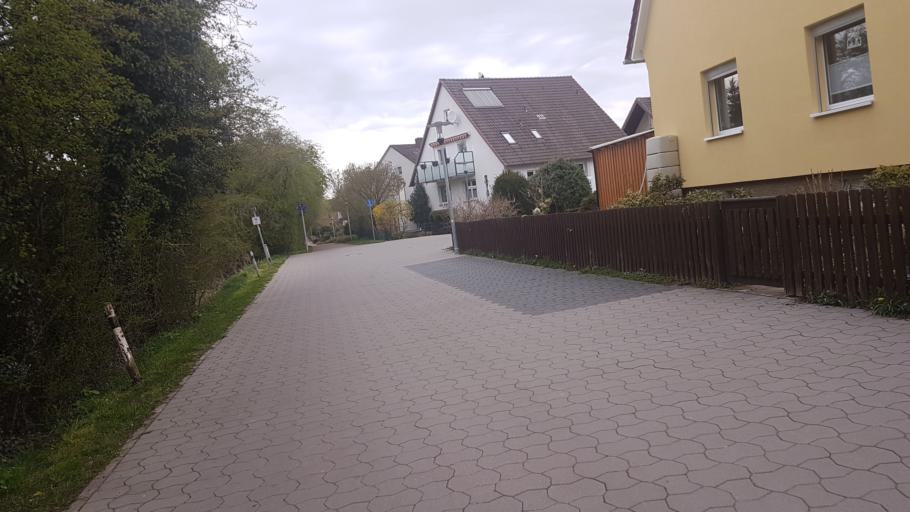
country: DE
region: Lower Saxony
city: Hameln
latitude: 52.1142
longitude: 9.3564
